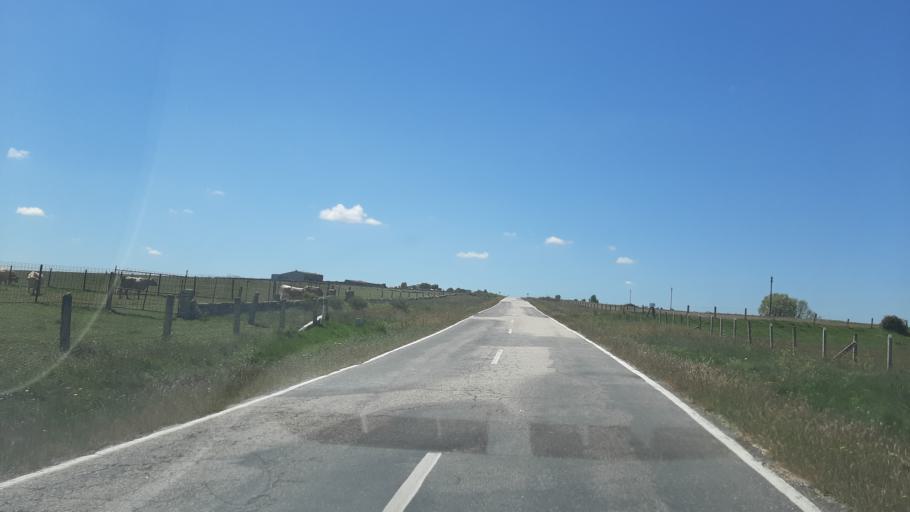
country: ES
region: Castille and Leon
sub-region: Provincia de Salamanca
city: Vitigudino
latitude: 41.0221
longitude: -6.4156
